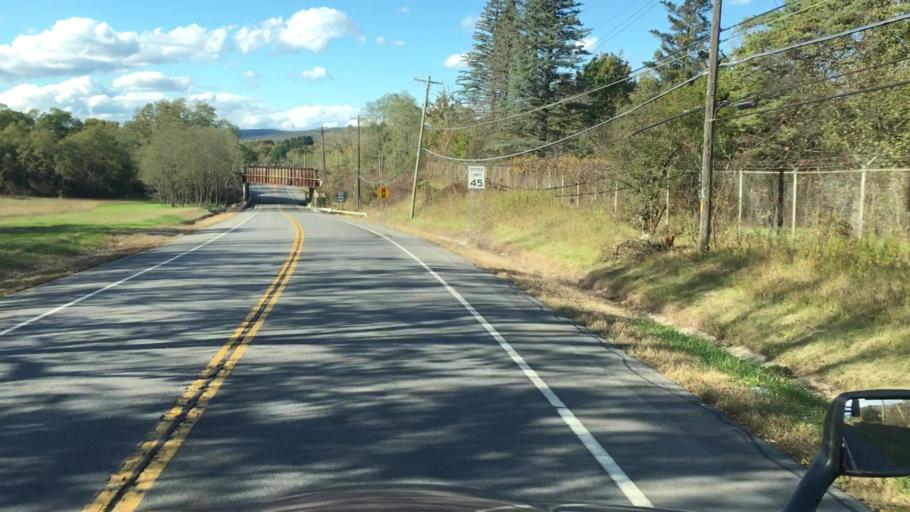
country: US
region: New York
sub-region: Schenectady County
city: Scotia
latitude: 42.8490
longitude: -74.0006
